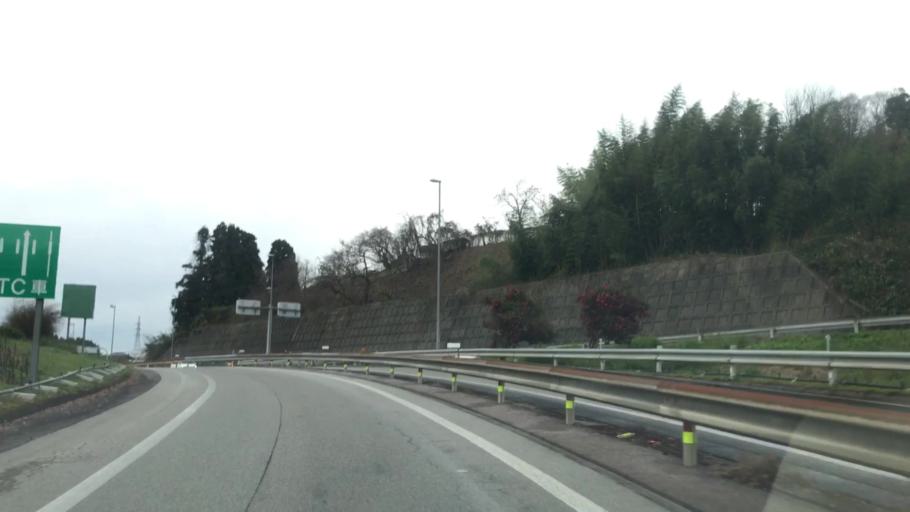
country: JP
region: Toyama
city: Kuragaki-kosugi
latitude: 36.6912
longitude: 137.0806
